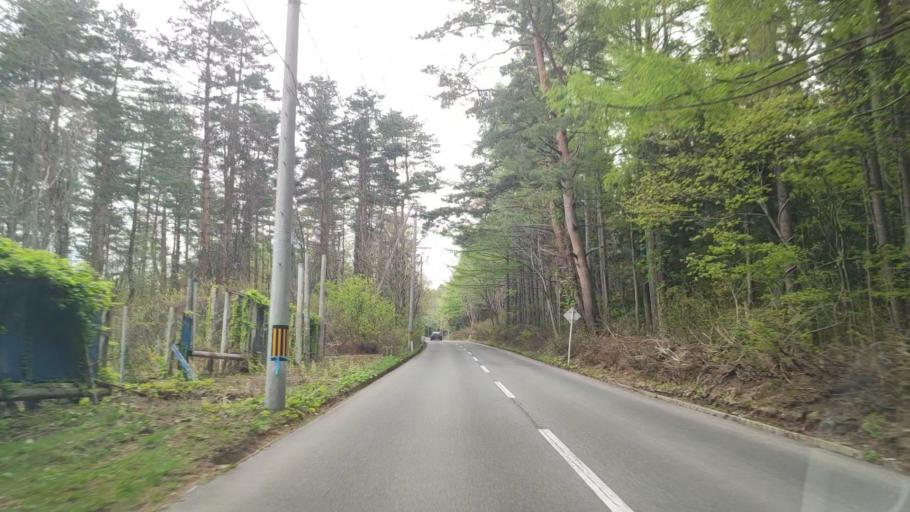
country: JP
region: Aomori
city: Aomori Shi
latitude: 40.7466
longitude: 140.8221
